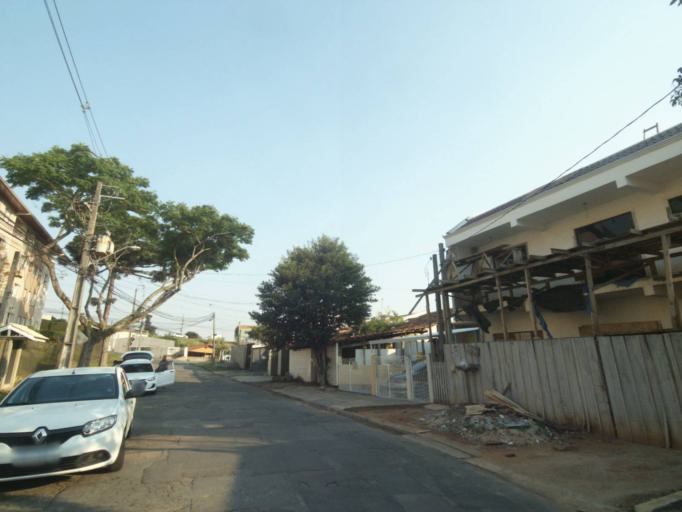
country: BR
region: Parana
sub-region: Sao Jose Dos Pinhais
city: Sao Jose dos Pinhais
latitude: -25.5291
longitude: -49.2558
